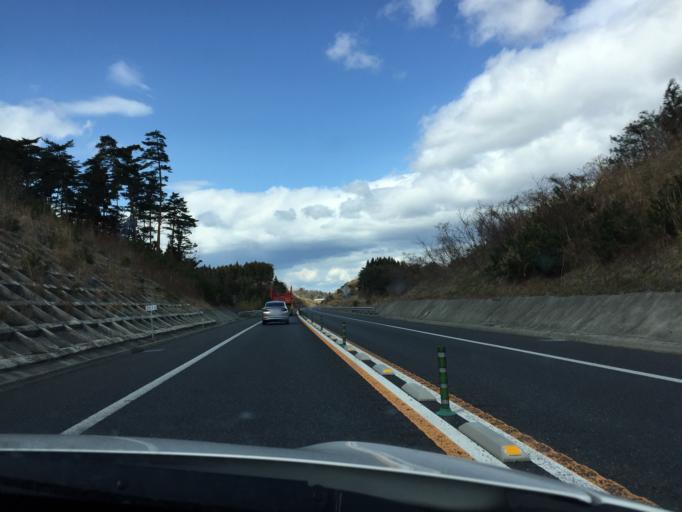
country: JP
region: Miyagi
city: Marumori
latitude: 37.7487
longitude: 140.9033
